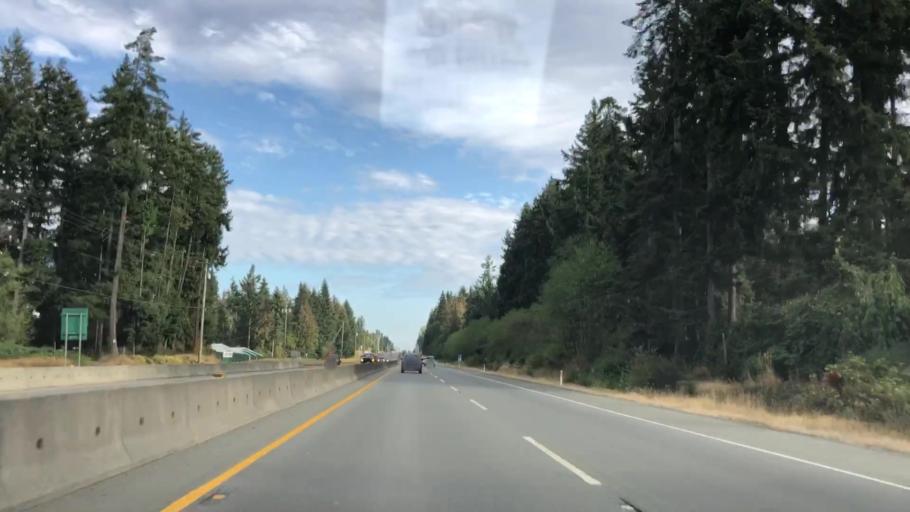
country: CA
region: British Columbia
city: Duncan
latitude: 48.7018
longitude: -123.5998
